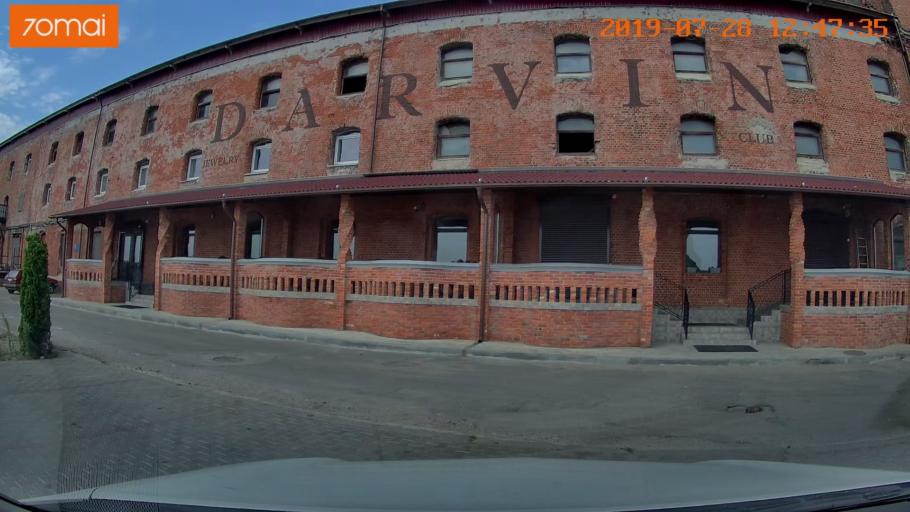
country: RU
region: Kaliningrad
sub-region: Gorod Kaliningrad
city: Kaliningrad
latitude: 54.7046
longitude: 20.4540
